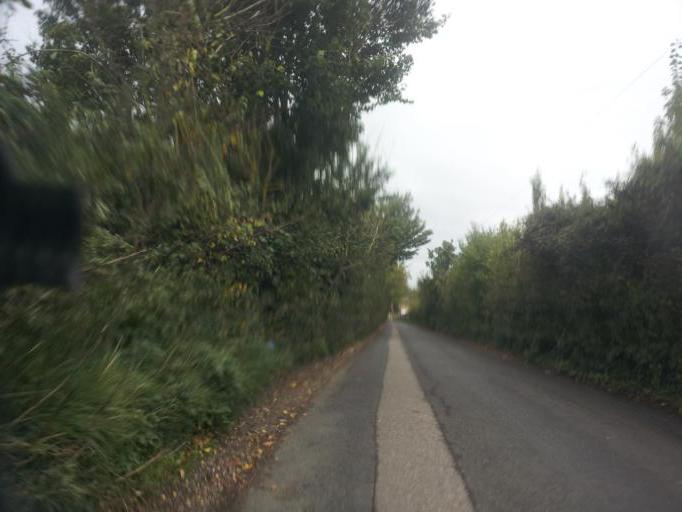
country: GB
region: England
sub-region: Kent
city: Teynham
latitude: 51.3401
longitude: 0.7711
